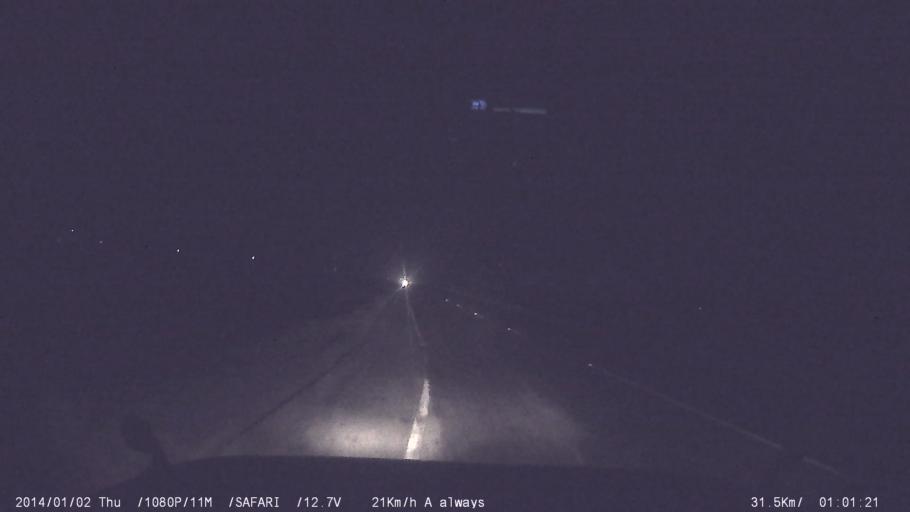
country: IN
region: Tamil Nadu
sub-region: Coimbatore
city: Madukkarai
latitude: 10.8956
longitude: 76.9471
